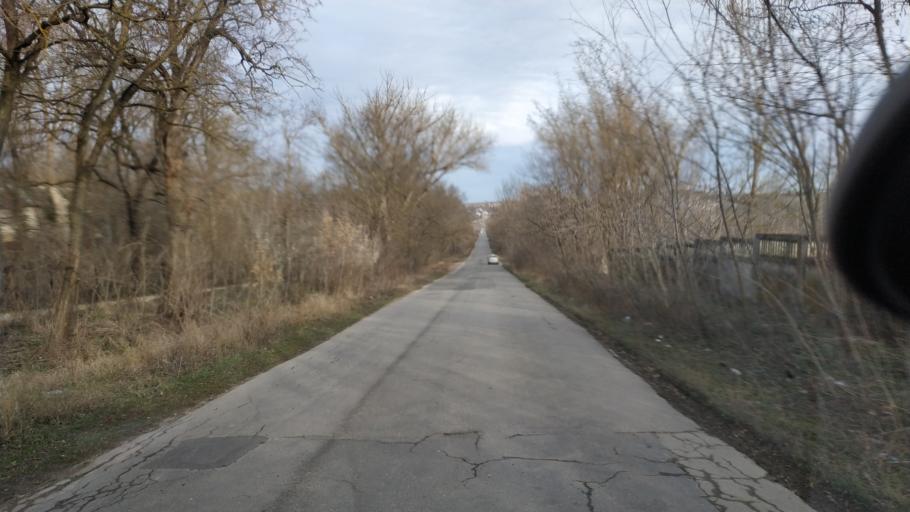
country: MD
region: Chisinau
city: Vadul lui Voda
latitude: 47.1048
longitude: 29.0650
